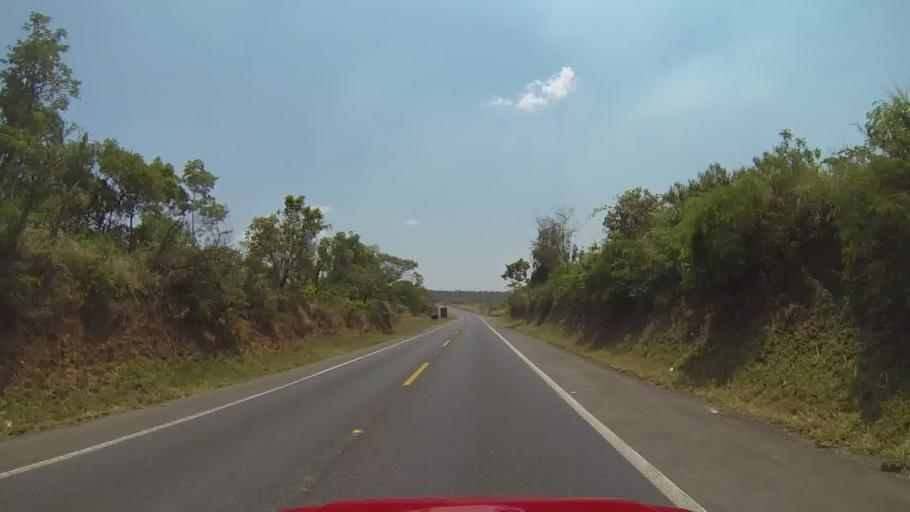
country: BR
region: Minas Gerais
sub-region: Formiga
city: Formiga
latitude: -20.3499
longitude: -45.3106
